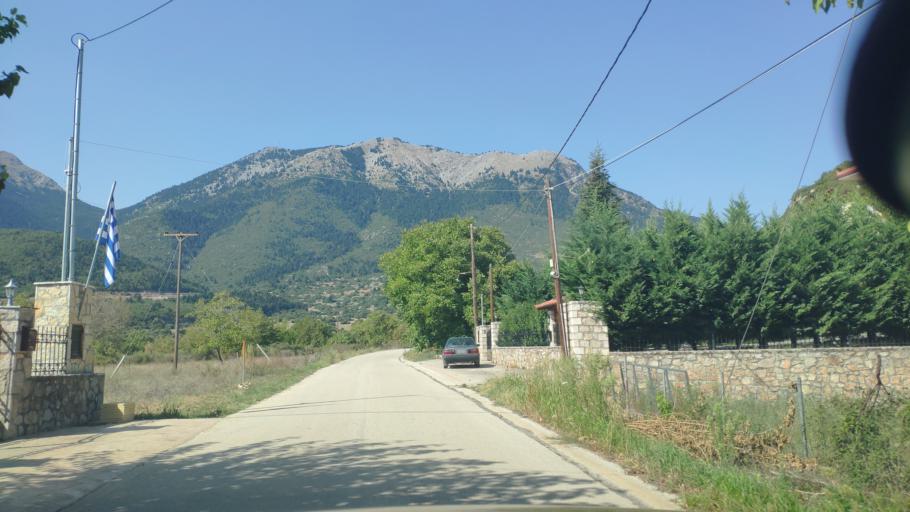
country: GR
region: Peloponnese
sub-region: Nomos Korinthias
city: Nemea
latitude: 37.8451
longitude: 22.4040
